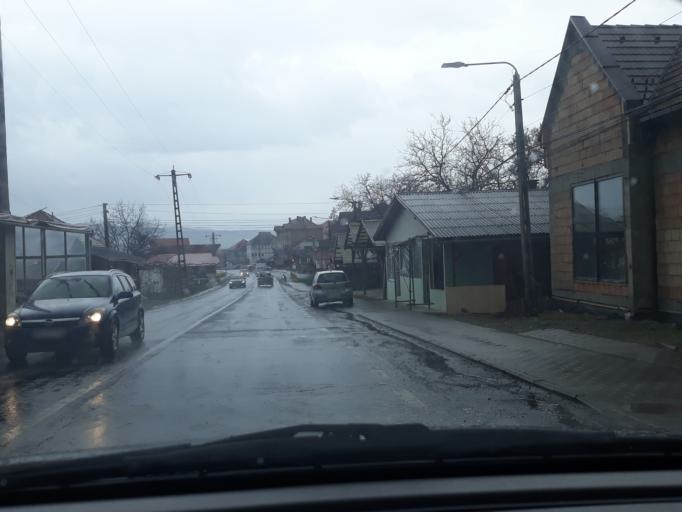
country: RO
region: Harghita
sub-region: Comuna Corund
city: Corund
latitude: 46.4710
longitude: 25.1864
